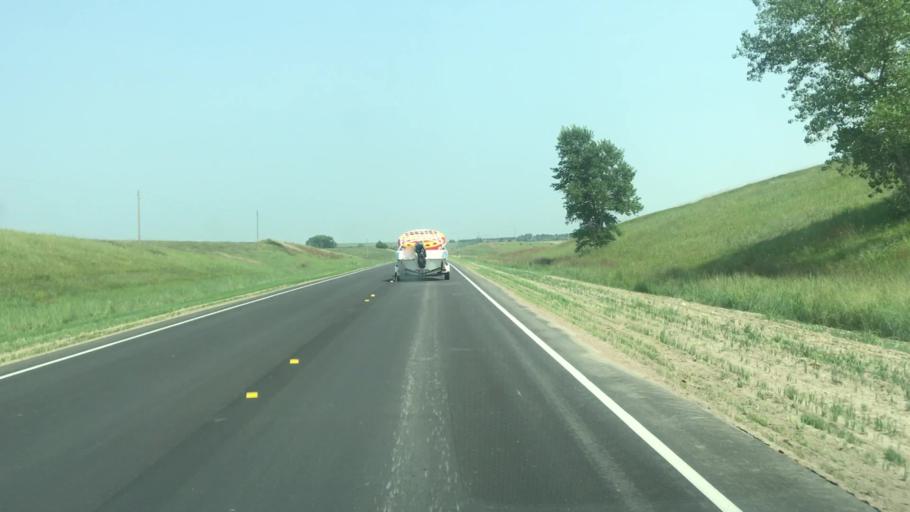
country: US
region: Nebraska
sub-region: Sherman County
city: Loup City
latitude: 41.2632
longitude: -98.9286
